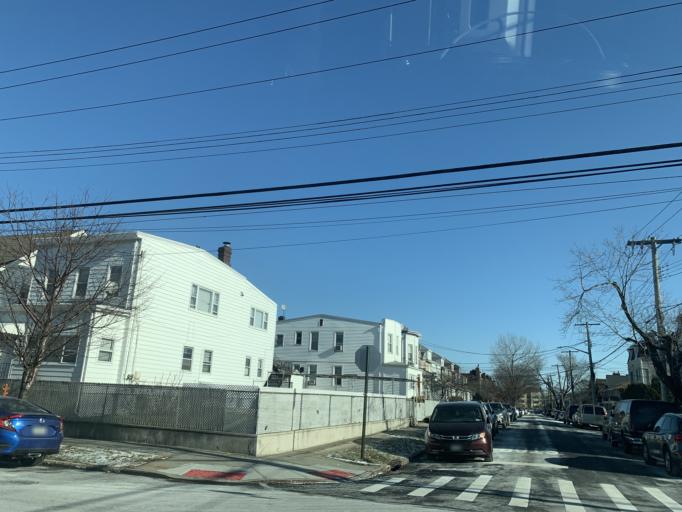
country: US
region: New York
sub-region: Nassau County
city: East Atlantic Beach
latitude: 40.7851
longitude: -73.8165
